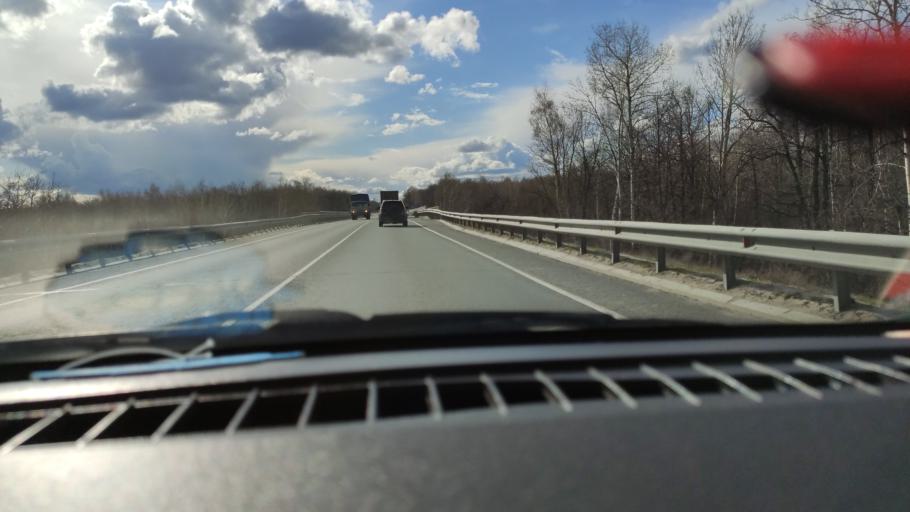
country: RU
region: Saratov
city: Vol'sk
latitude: 52.1092
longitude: 47.3751
